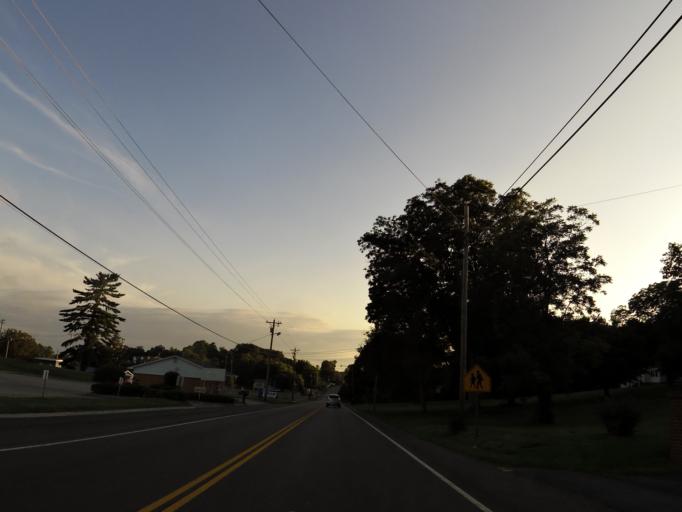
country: US
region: Tennessee
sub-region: Jefferson County
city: Dandridge
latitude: 36.0231
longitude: -83.4055
